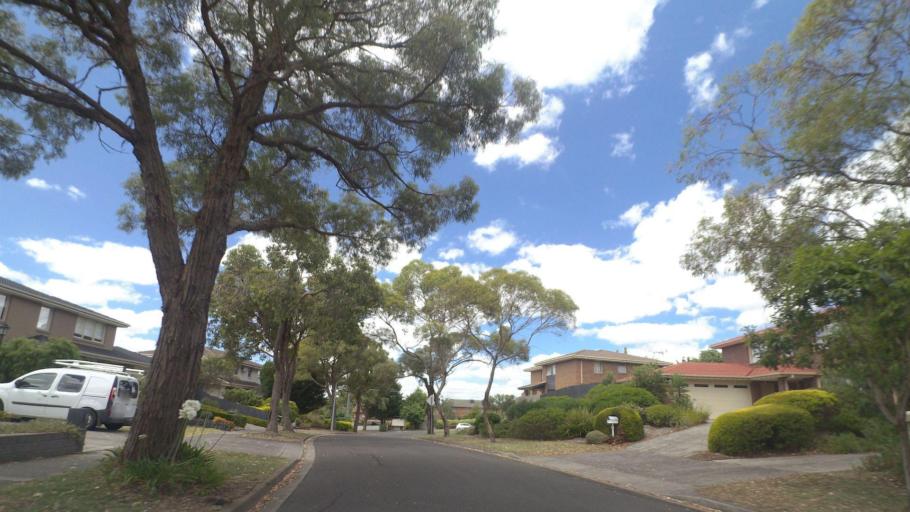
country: AU
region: Victoria
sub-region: Maroondah
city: Warranwood
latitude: -37.7716
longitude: 145.2438
